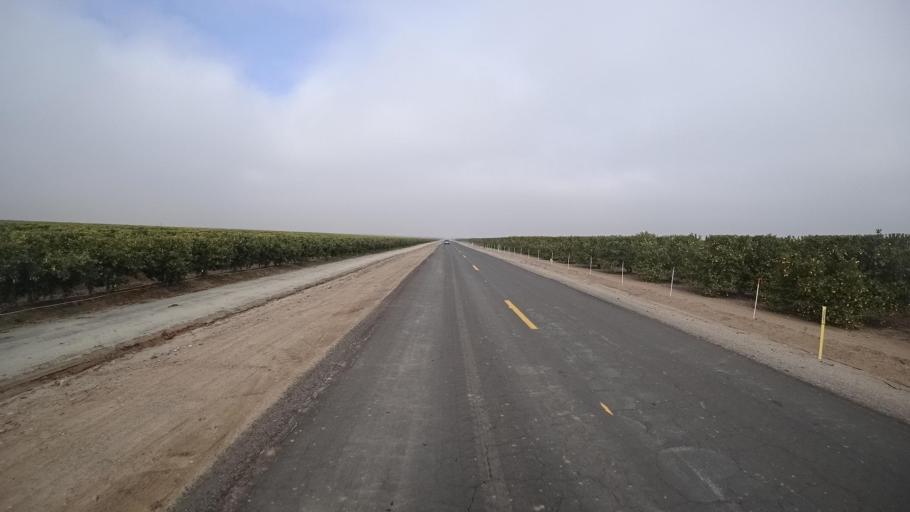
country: US
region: California
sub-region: Kern County
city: Maricopa
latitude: 35.0627
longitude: -119.3137
